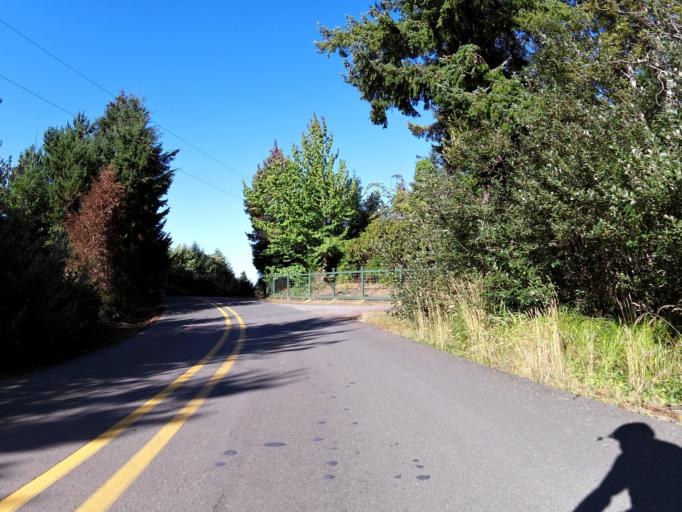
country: US
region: Oregon
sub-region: Coos County
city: Bandon
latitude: 43.0396
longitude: -124.4027
